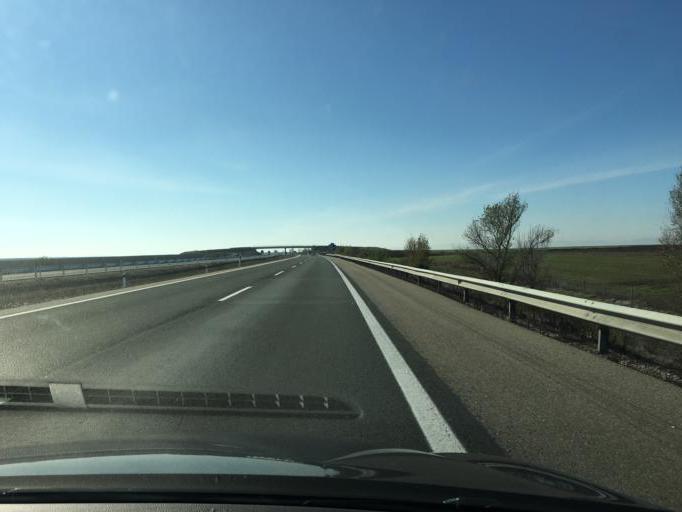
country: ES
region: Castille and Leon
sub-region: Provincia de Burgos
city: Grisalena
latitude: 42.5825
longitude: -3.2478
